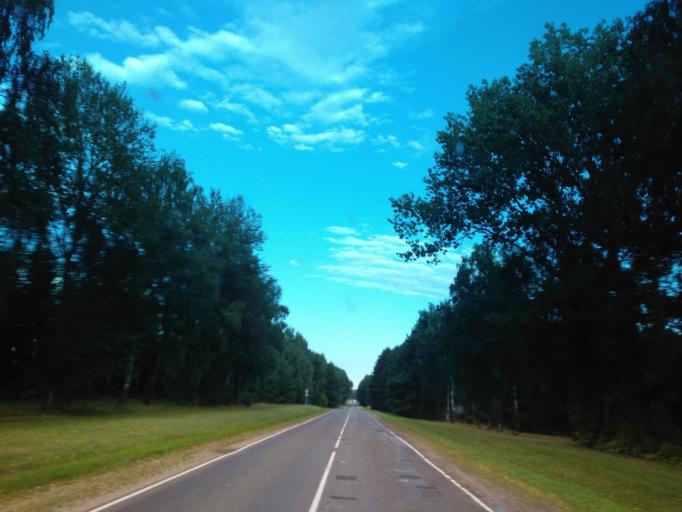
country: BY
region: Minsk
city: Uzda
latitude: 53.4221
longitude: 27.3970
